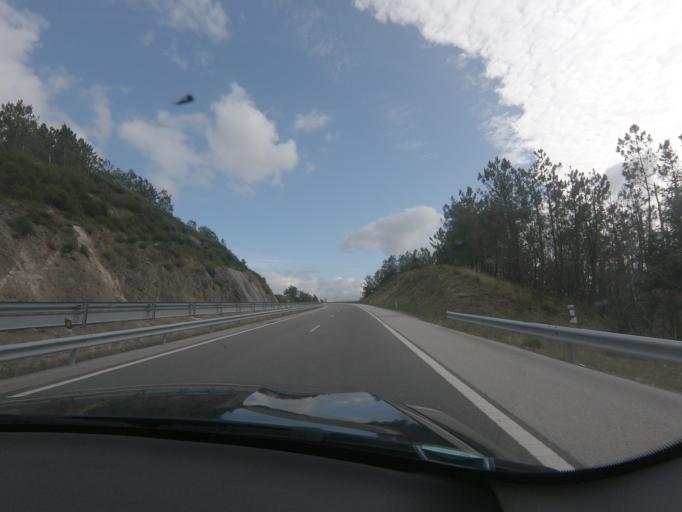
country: PT
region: Viseu
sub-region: Lamego
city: Lamego
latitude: 41.0458
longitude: -7.8600
